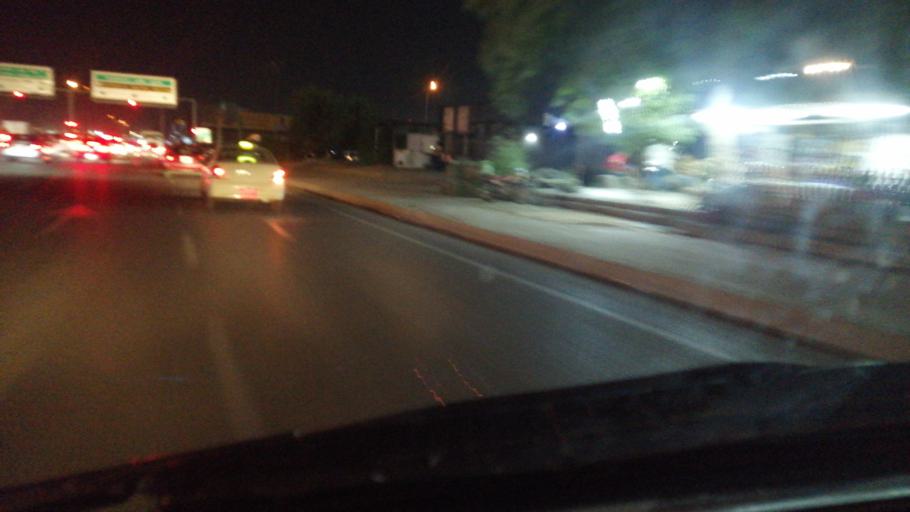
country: IQ
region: Arbil
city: Erbil
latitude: 36.1580
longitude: 43.9919
